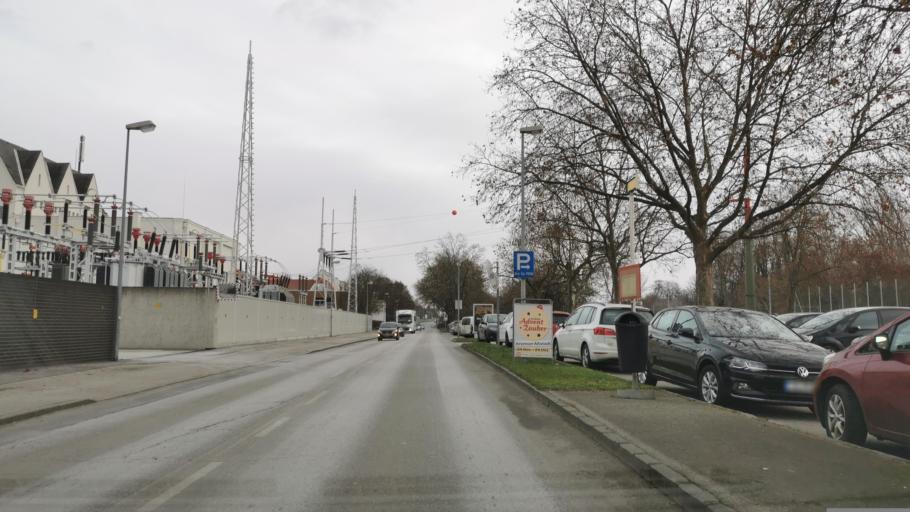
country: AT
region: Lower Austria
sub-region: Politischer Bezirk Krems
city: Weinzierl bei Krems
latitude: 48.4063
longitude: 15.6056
